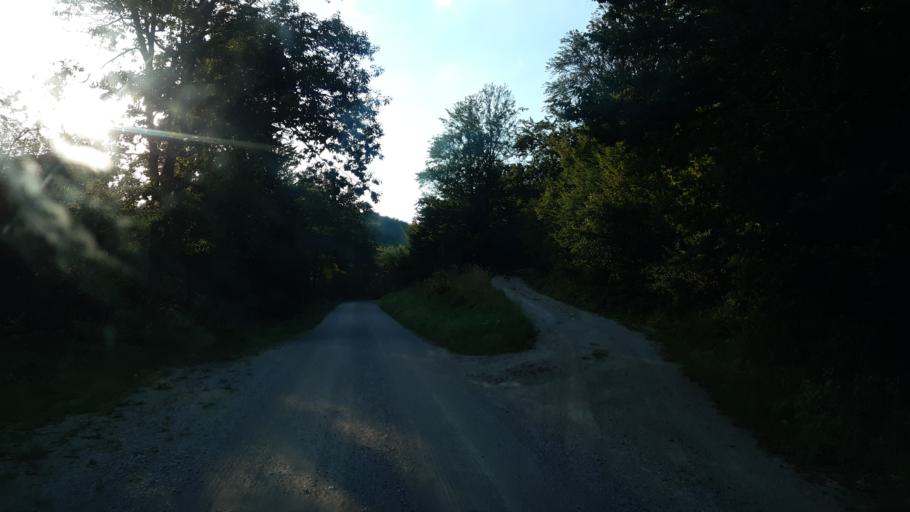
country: SI
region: Kocevje
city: Kocevje
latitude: 45.6668
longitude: 14.9574
